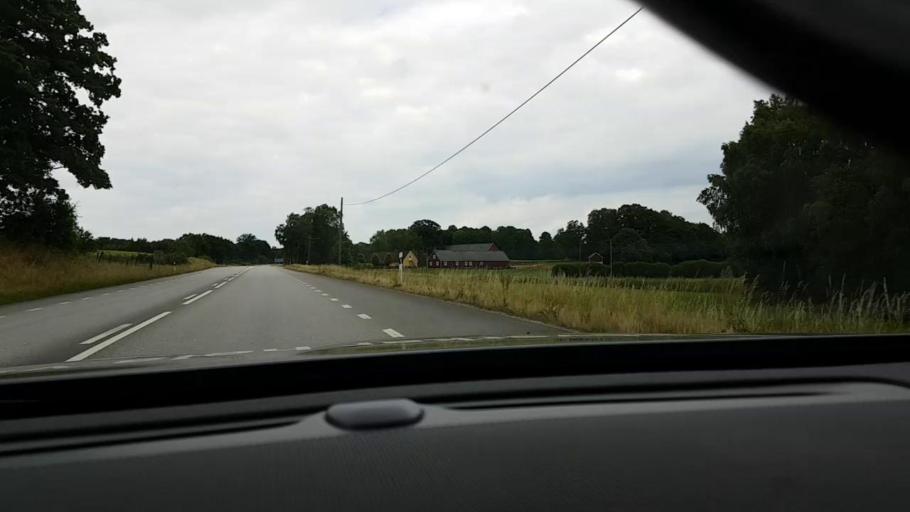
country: SE
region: Skane
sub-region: Hassleholms Kommun
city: Tormestorp
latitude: 56.0718
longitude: 13.7429
